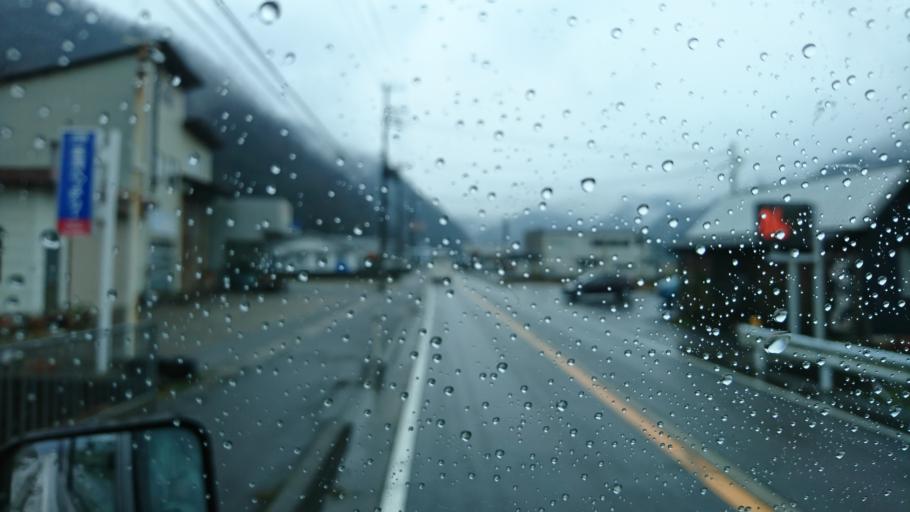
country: JP
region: Tottori
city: Tottori
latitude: 35.5798
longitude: 134.4895
